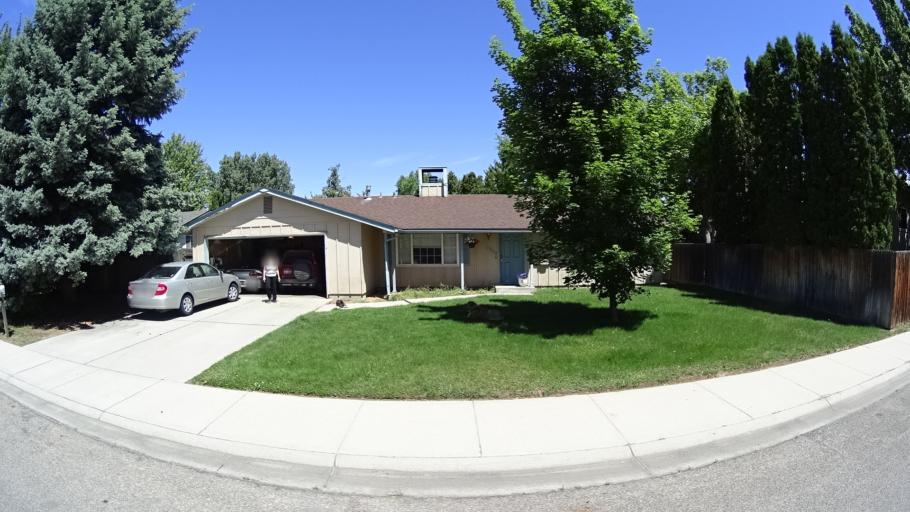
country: US
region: Idaho
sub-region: Ada County
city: Boise
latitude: 43.5678
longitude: -116.1677
